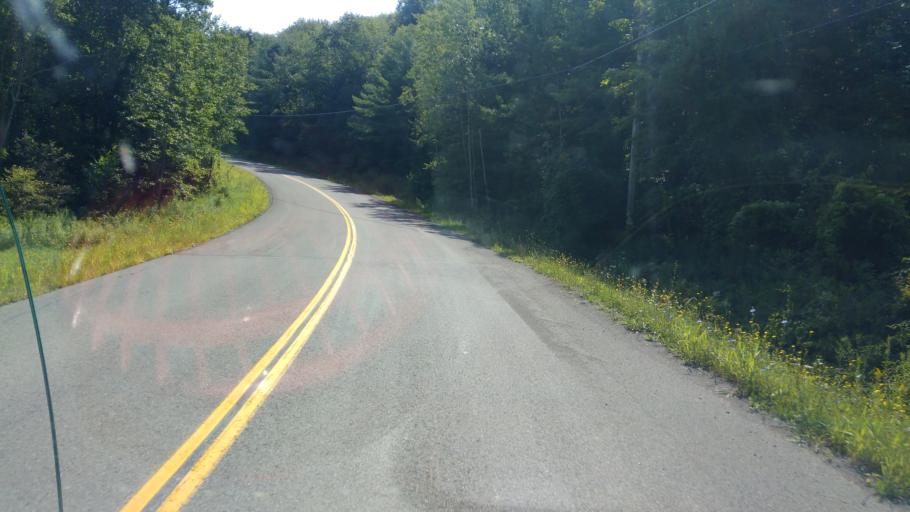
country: US
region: New York
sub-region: Allegany County
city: Belmont
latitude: 42.2912
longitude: -78.0015
